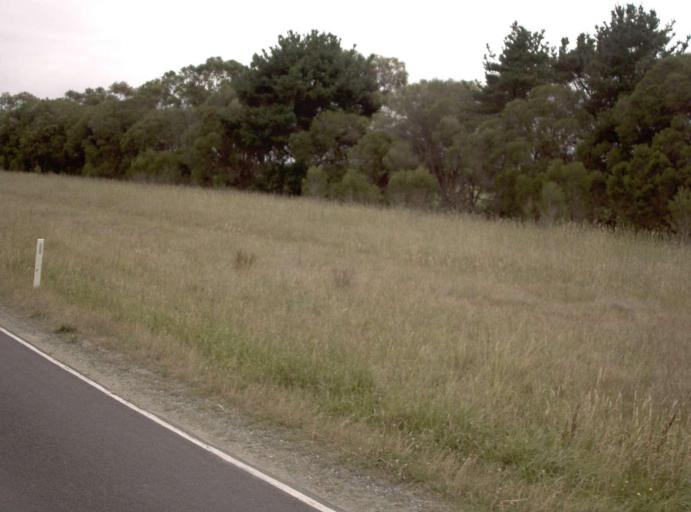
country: AU
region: Victoria
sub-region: Wellington
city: Heyfield
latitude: -38.0269
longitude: 146.7656
